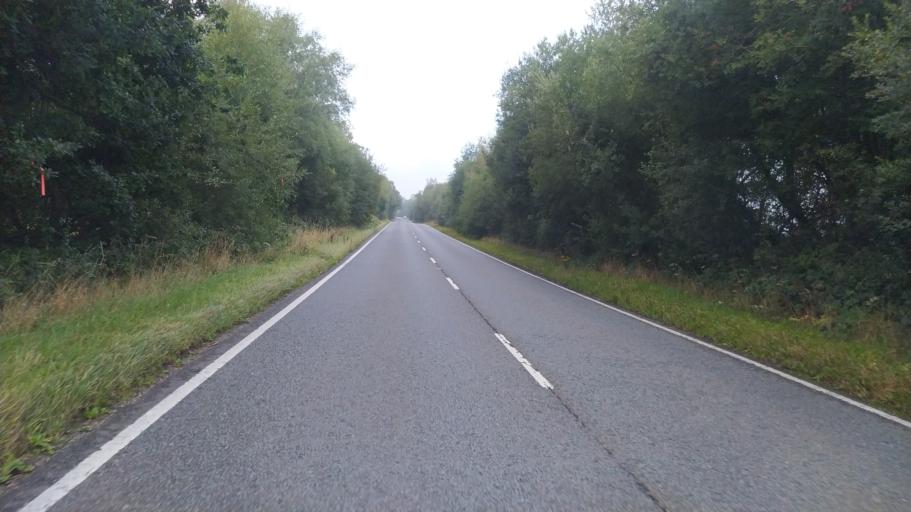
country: GB
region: England
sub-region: Hampshire
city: New Milton
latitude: 50.7894
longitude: -1.6884
